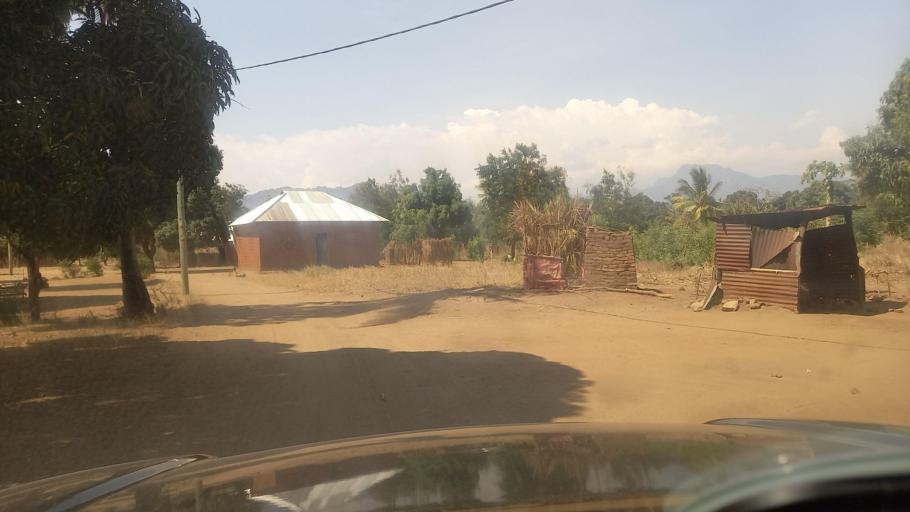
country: TZ
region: Morogoro
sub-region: Kilosa
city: Magole
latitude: -6.3478
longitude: 37.3996
